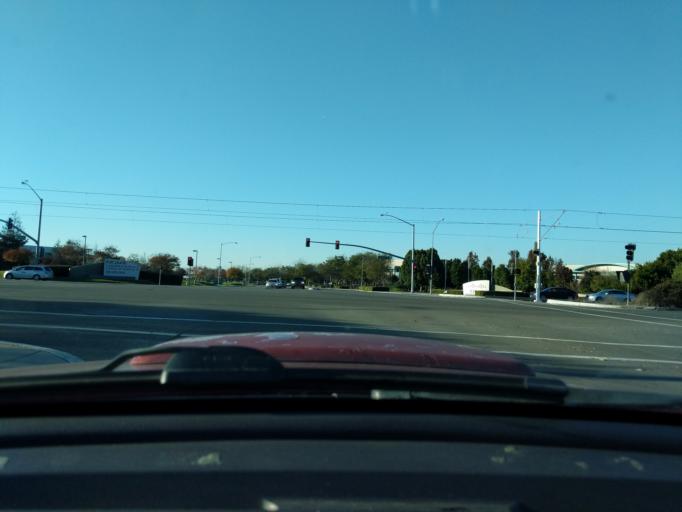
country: US
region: California
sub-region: Santa Clara County
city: Milpitas
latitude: 37.4136
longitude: -121.9164
